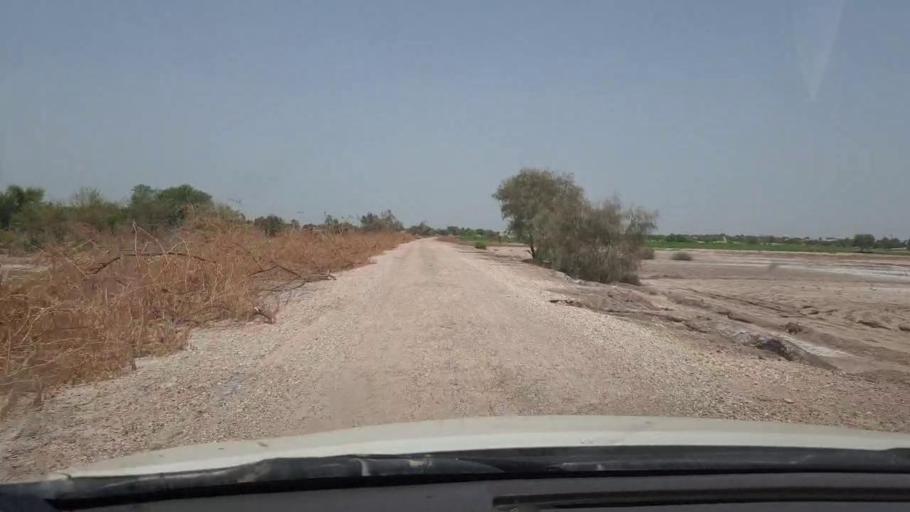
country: PK
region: Sindh
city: Rohri
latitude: 27.5097
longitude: 69.1845
